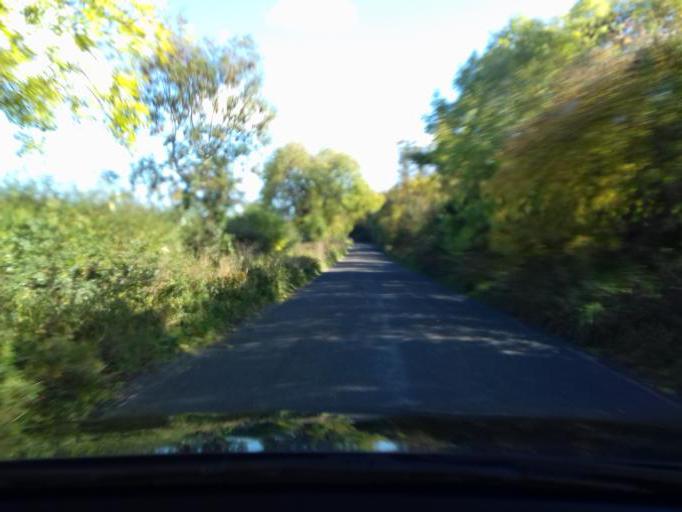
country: IE
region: Leinster
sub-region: An Mhi
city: Slane
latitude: 53.6851
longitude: -6.4805
